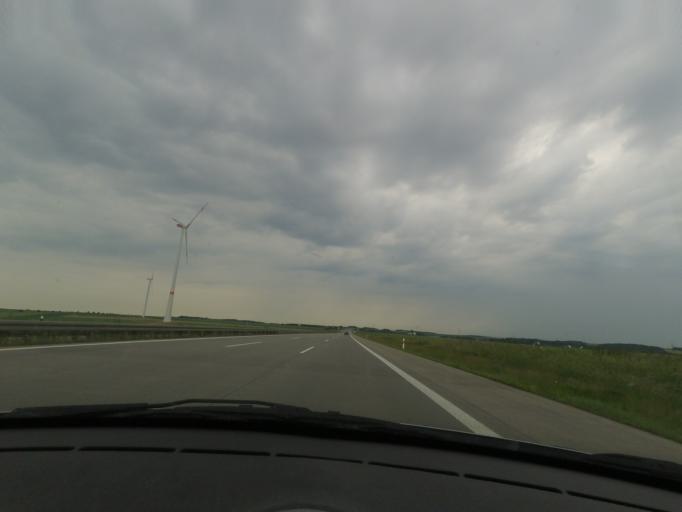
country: DE
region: Thuringia
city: Heyersdorf
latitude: 50.8384
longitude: 12.3622
